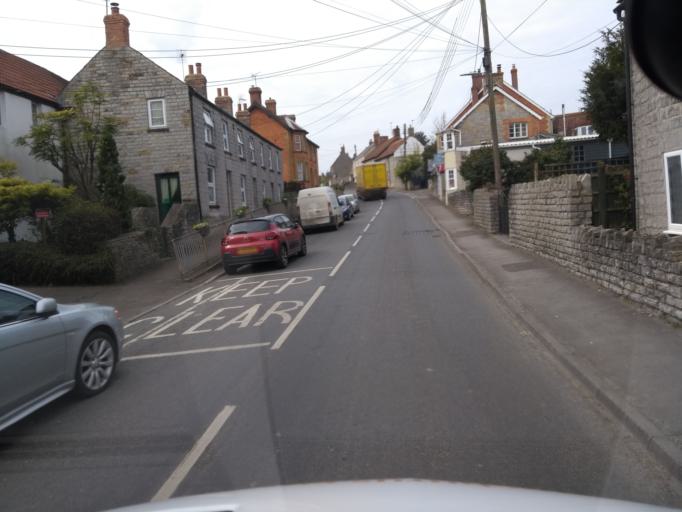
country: GB
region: England
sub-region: Somerset
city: Curry Rivel
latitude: 51.0228
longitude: -2.8691
